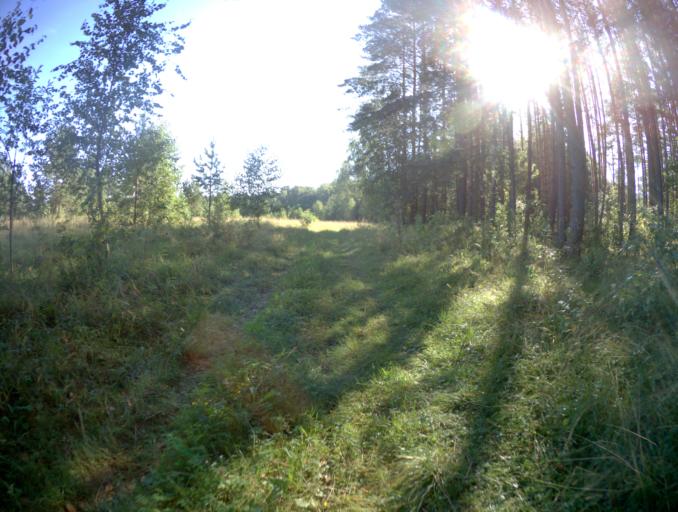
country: RU
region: Vladimir
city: Nikologory
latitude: 56.1720
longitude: 41.9474
